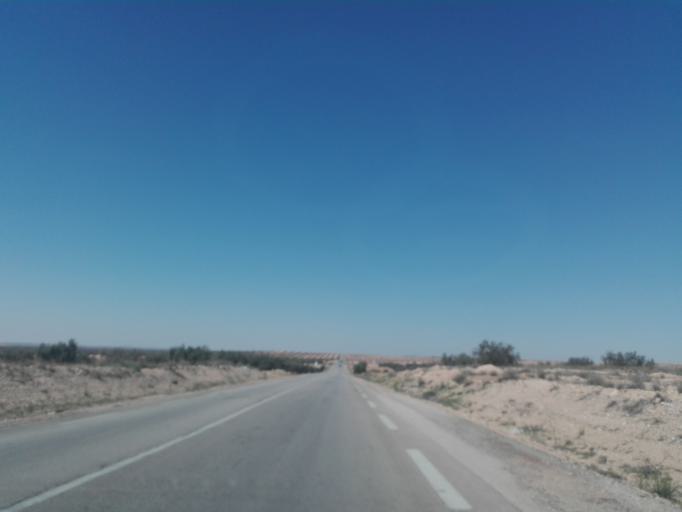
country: TN
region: Safaqis
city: Bi'r `Ali Bin Khalifah
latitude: 34.7589
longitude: 10.3014
